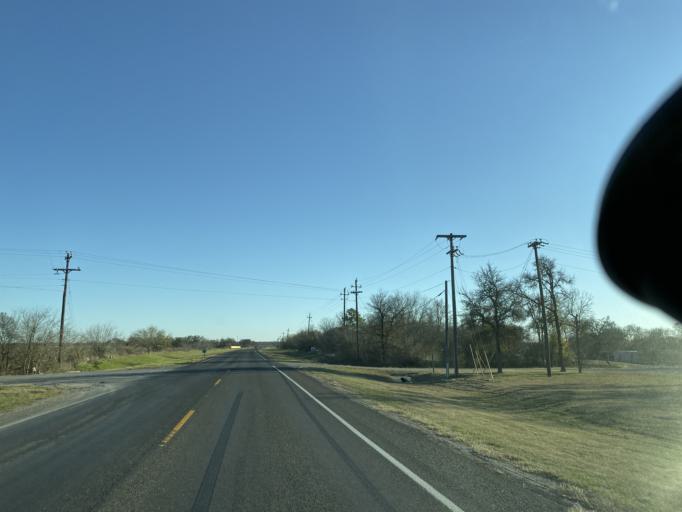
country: US
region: Texas
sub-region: Bastrop County
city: Wyldwood
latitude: 30.0980
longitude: -97.5055
